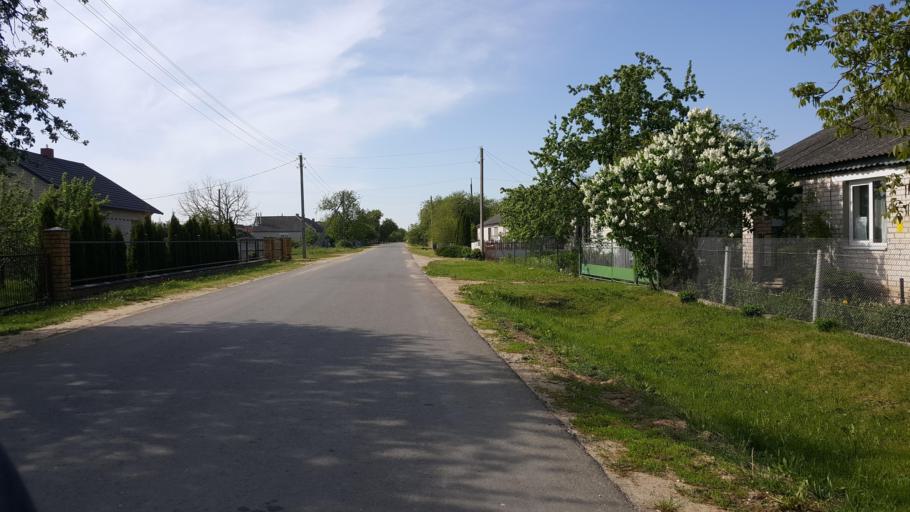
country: BY
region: Brest
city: Kamyanyets
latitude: 52.3264
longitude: 23.7787
